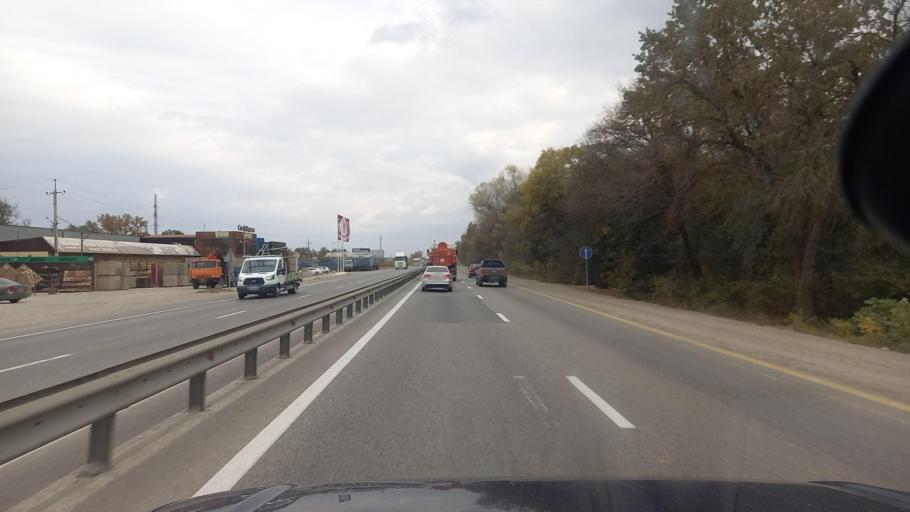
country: RU
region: Krasnodarskiy
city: Afipskiy
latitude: 44.9048
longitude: 38.8758
